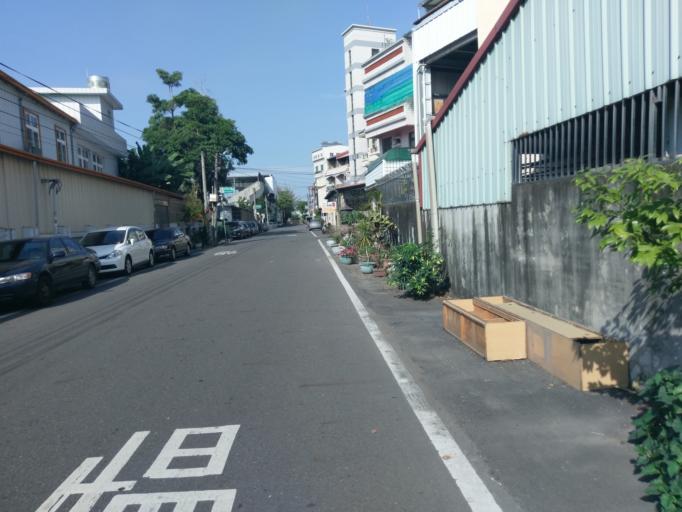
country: TW
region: Taiwan
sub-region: Yunlin
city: Douliu
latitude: 23.7124
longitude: 120.5530
